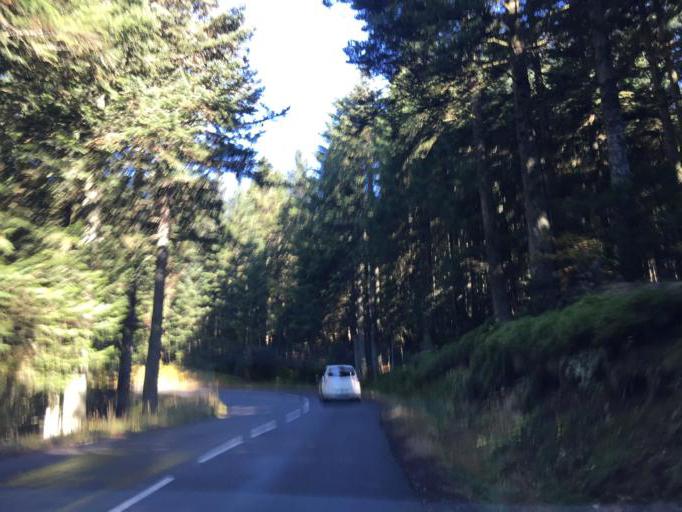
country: FR
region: Rhone-Alpes
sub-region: Departement de la Loire
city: Bourg-Argental
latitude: 45.3715
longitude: 4.5455
